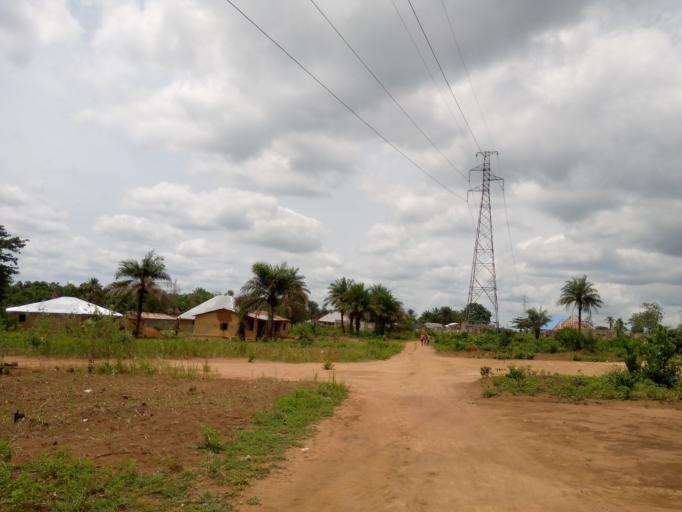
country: SL
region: Western Area
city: Waterloo
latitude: 8.3311
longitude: -13.0132
